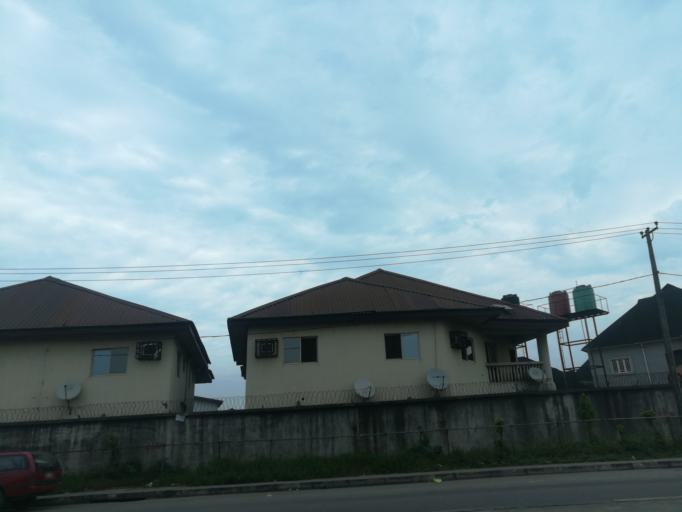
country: NG
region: Rivers
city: Port Harcourt
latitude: 4.8337
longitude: 6.9762
